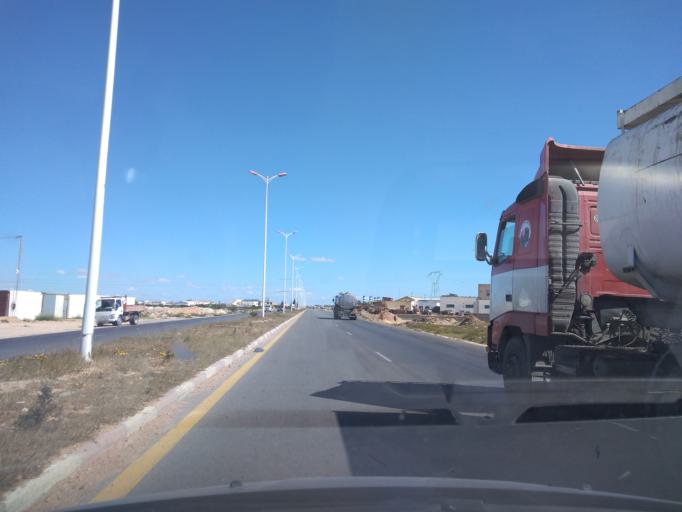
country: TN
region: Safaqis
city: Sfax
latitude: 34.8052
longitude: 10.6905
